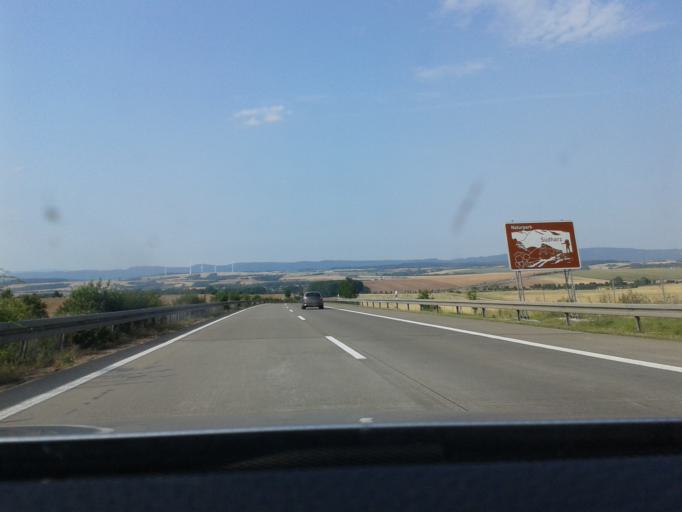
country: DE
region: Thuringia
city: Wipperdorf
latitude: 51.4679
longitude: 10.6884
